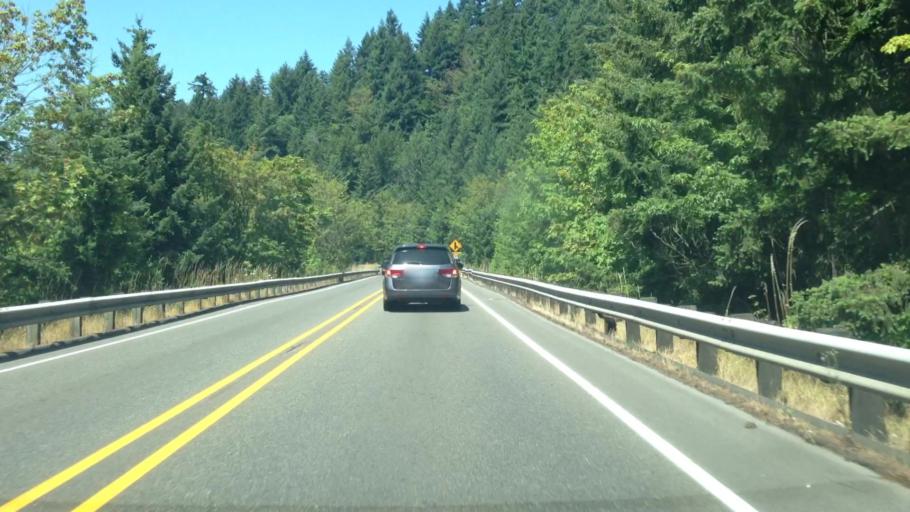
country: US
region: Washington
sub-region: Pierce County
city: North Puyallup
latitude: 47.2133
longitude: -122.2939
